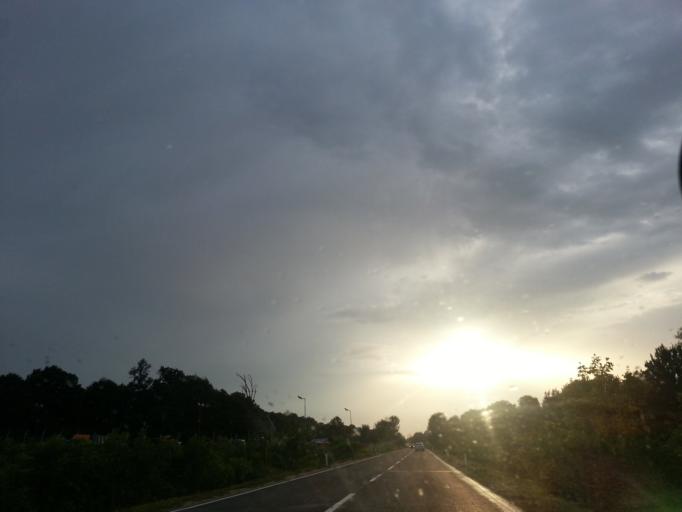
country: HR
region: Vukovarsko-Srijemska
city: Gunja
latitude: 44.8481
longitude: 18.9255
